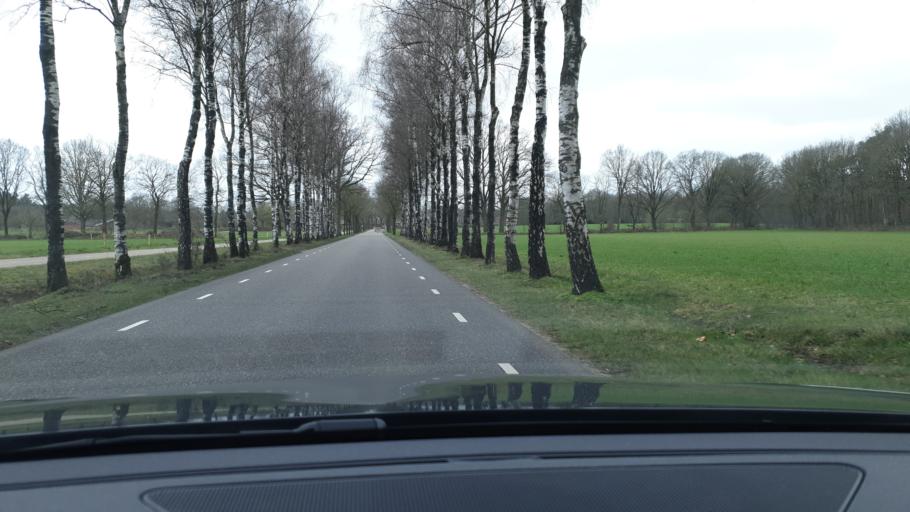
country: NL
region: North Brabant
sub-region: Gemeente Veldhoven
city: Oerle
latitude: 51.4050
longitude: 5.3539
